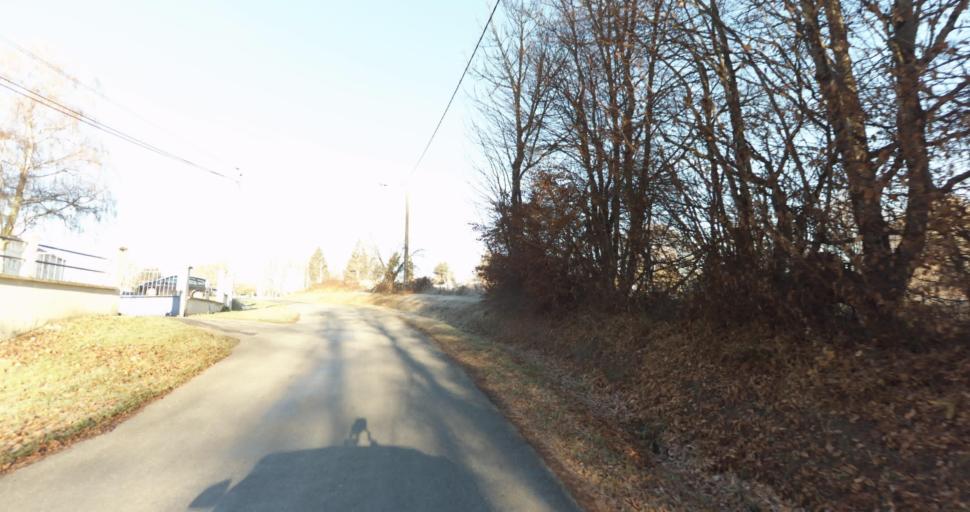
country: FR
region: Limousin
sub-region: Departement de la Haute-Vienne
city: Aixe-sur-Vienne
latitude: 45.8111
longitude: 1.1383
